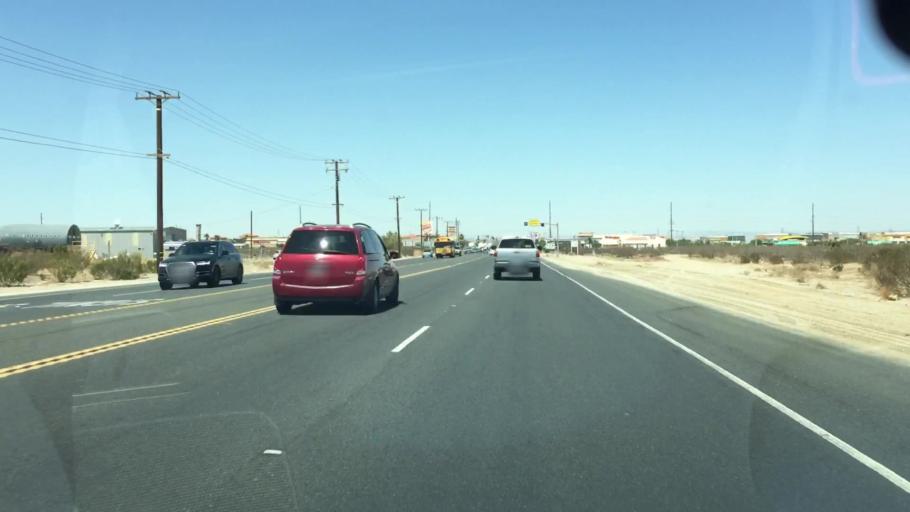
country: US
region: California
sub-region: San Bernardino County
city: Mountain View Acres
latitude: 34.5027
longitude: -117.3994
